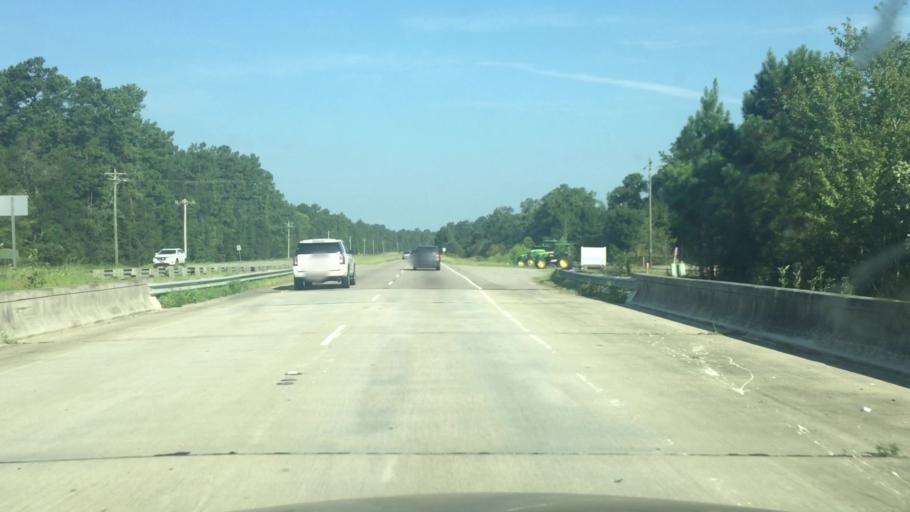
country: US
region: South Carolina
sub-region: Horry County
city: North Myrtle Beach
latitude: 33.9123
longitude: -78.7148
